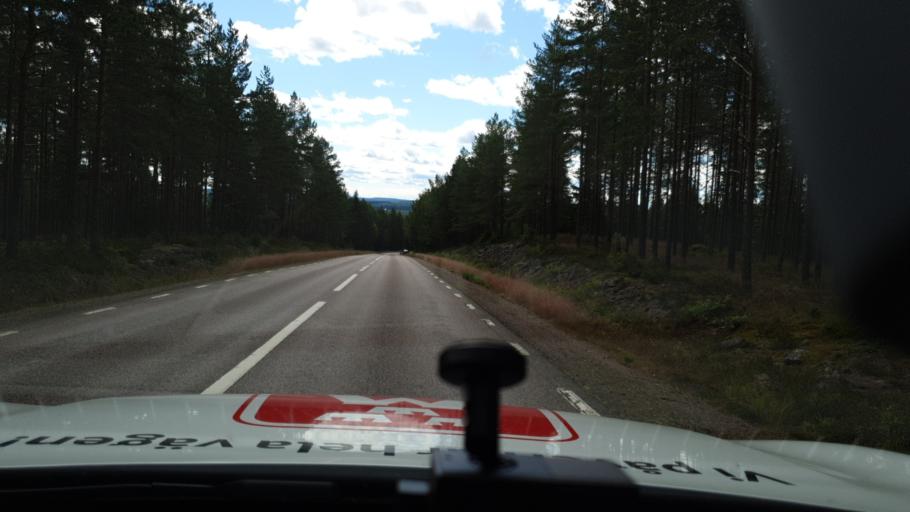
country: SE
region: Vaermland
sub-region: Sunne Kommun
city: Sunne
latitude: 59.6862
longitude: 13.0480
